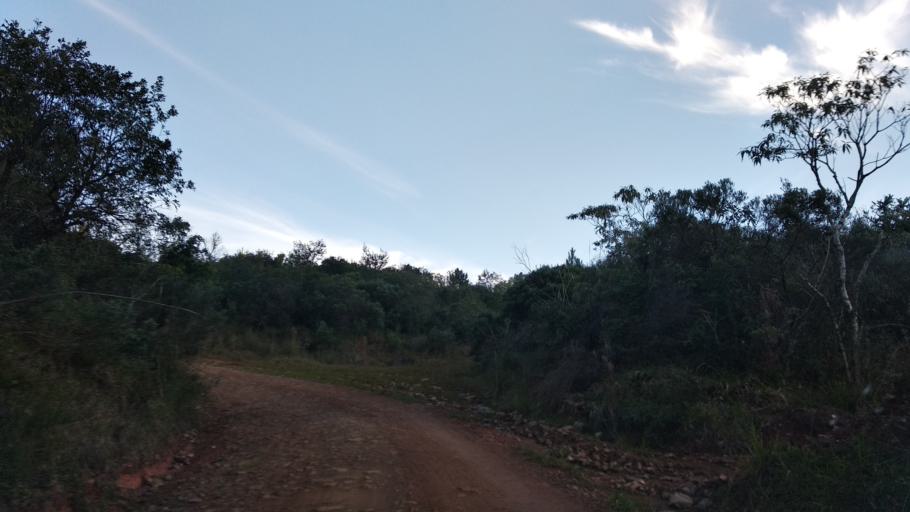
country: BR
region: Santa Catarina
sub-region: Celso Ramos
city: Celso Ramos
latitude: -27.5612
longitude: -51.2372
